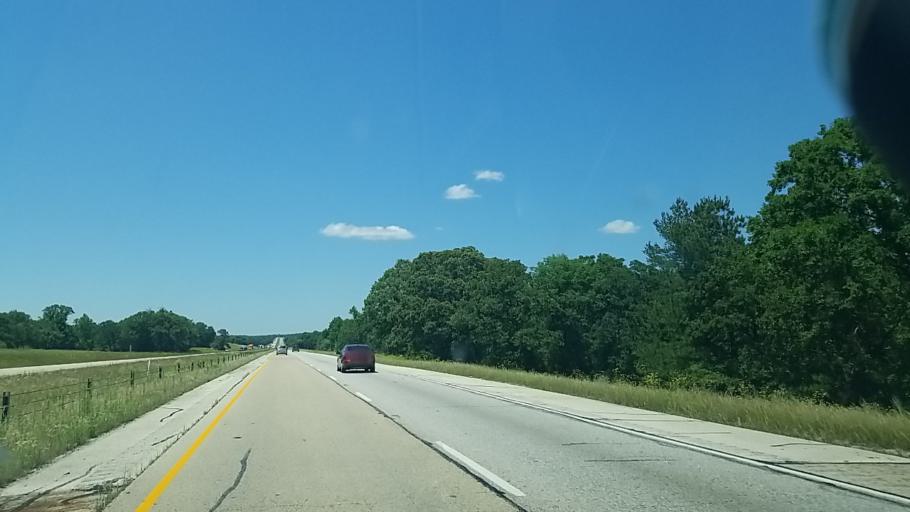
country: US
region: Texas
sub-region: Leon County
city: Centerville
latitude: 31.1702
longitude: -95.9877
